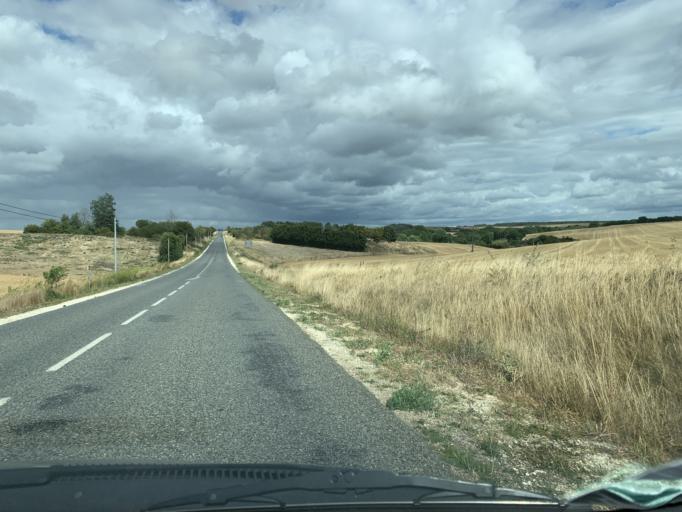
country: FR
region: Bourgogne
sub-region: Departement de la Nievre
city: Clamecy
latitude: 47.4313
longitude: 3.4801
